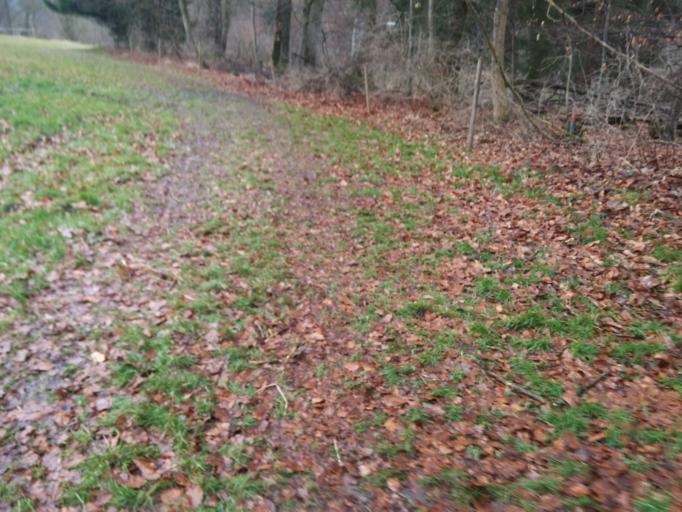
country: DE
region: Bavaria
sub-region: Swabia
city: Kronburg
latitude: 47.8698
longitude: 10.1742
